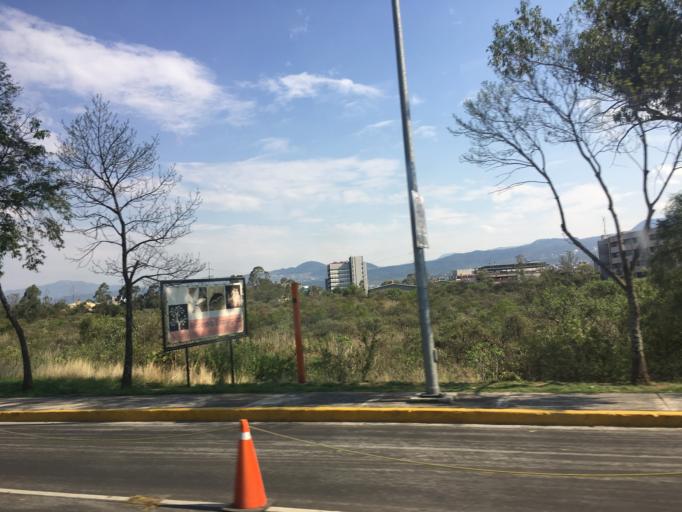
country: MX
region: Mexico City
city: Tlalpan
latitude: 19.3115
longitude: -99.1837
